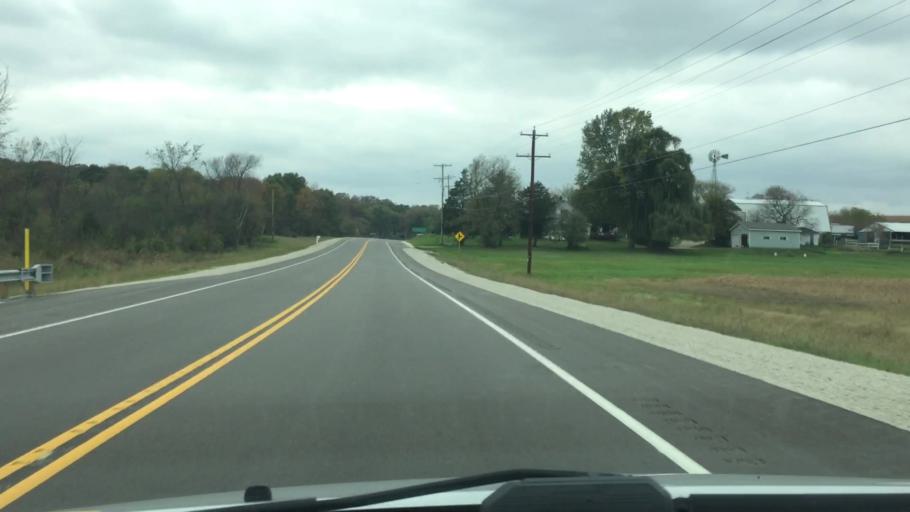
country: US
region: Wisconsin
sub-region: Walworth County
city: Whitewater
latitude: 42.8534
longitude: -88.7907
